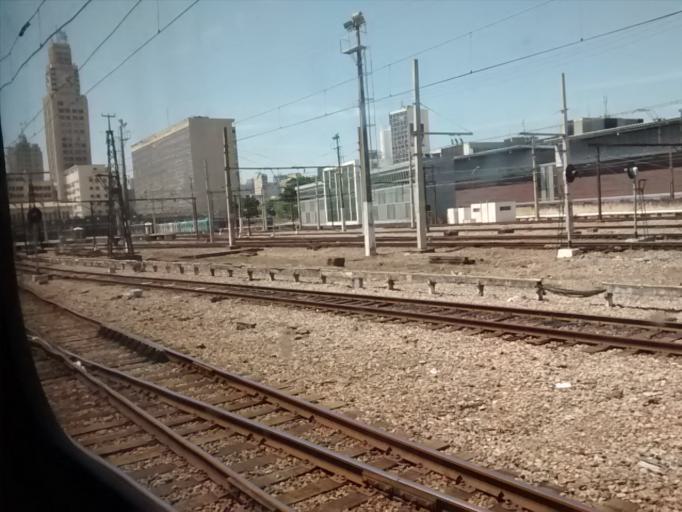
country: BR
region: Rio de Janeiro
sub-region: Rio De Janeiro
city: Rio de Janeiro
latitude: -22.9041
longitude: -43.1956
